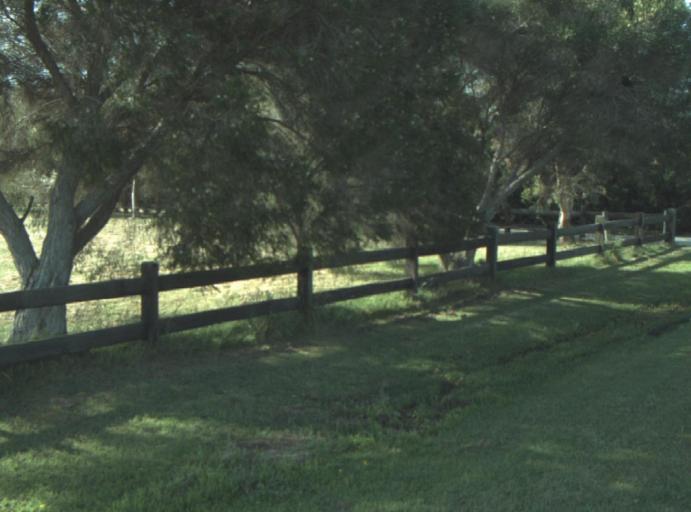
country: AU
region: Victoria
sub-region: Greater Geelong
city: Leopold
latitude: -38.1814
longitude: 144.4379
